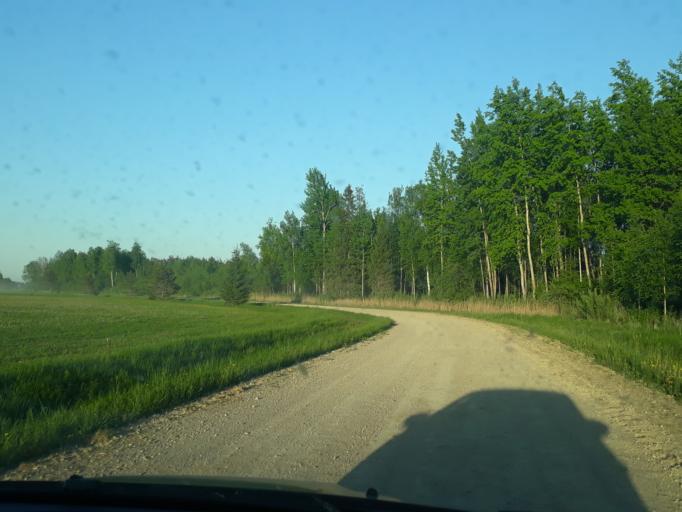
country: EE
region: Paernumaa
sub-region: Tootsi vald
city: Tootsi
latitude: 58.5796
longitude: 24.9158
